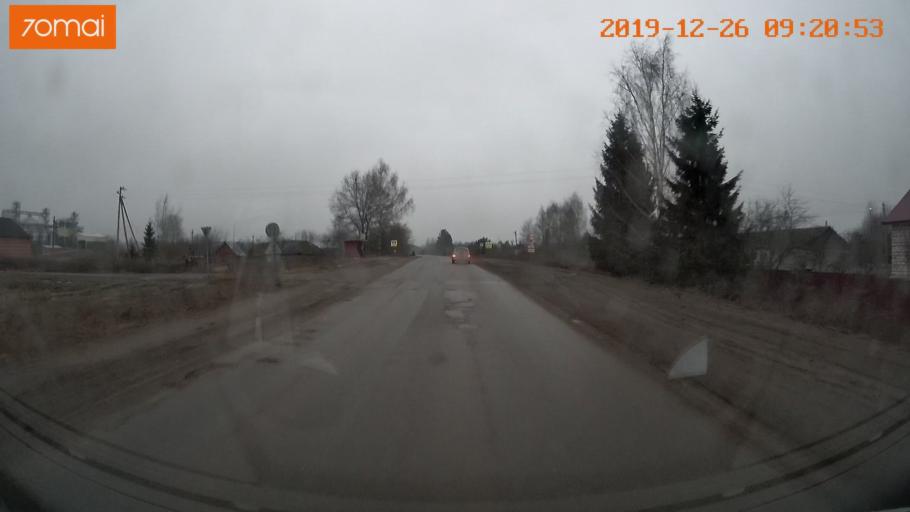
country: RU
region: Vologda
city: Gryazovets
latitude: 58.9654
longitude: 40.2273
